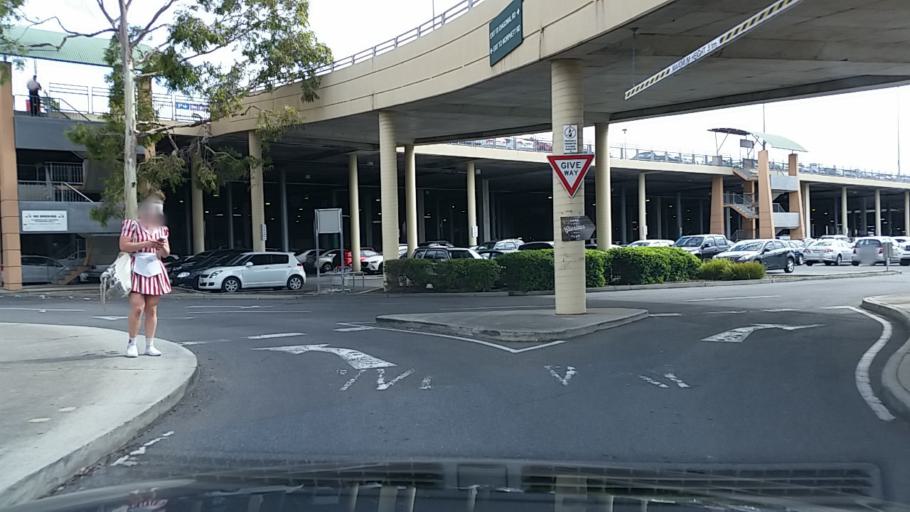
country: AU
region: South Australia
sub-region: Marion
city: Sturt
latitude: -35.0151
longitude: 138.5441
